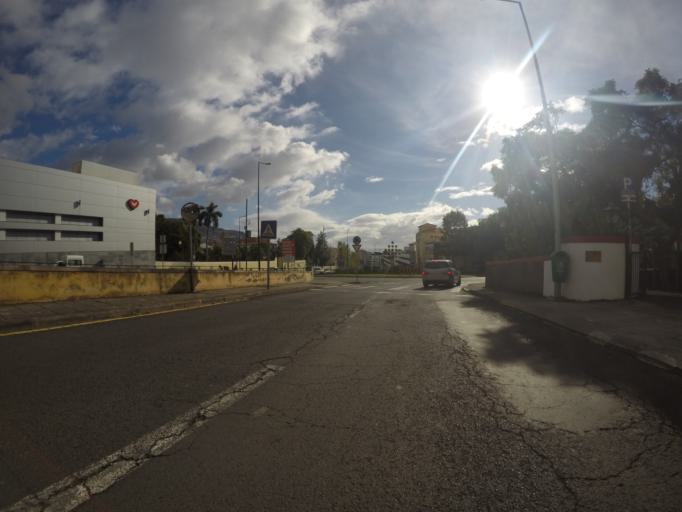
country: PT
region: Madeira
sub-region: Funchal
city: Funchal
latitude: 32.6487
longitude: -16.9176
